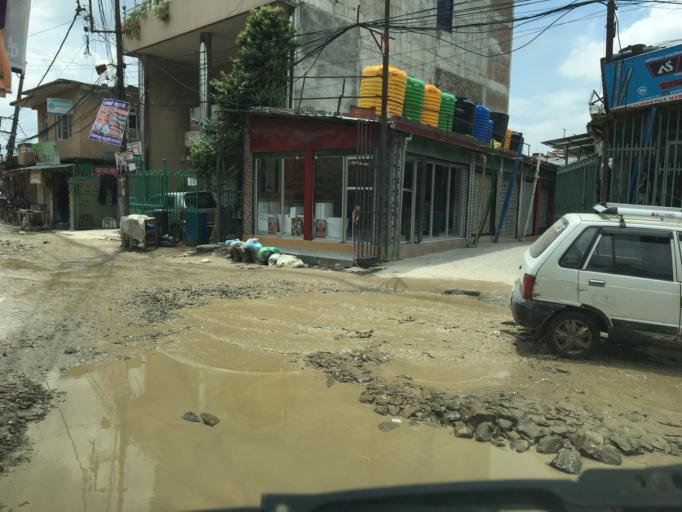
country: NP
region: Central Region
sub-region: Bagmati Zone
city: Kathmandu
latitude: 27.7285
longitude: 85.3519
